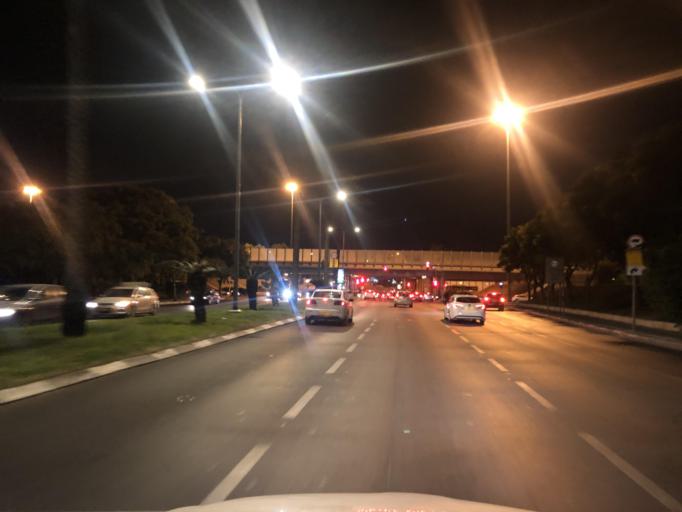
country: IL
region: Tel Aviv
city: Yafo
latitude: 32.0472
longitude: 34.7820
